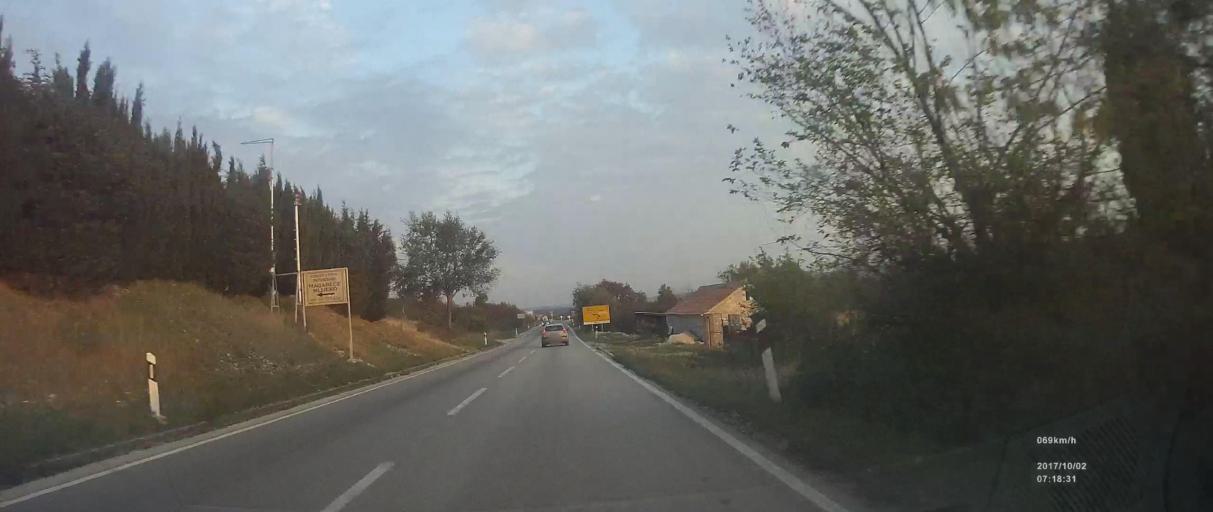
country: HR
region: Zadarska
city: Benkovac
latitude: 44.0185
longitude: 15.5936
